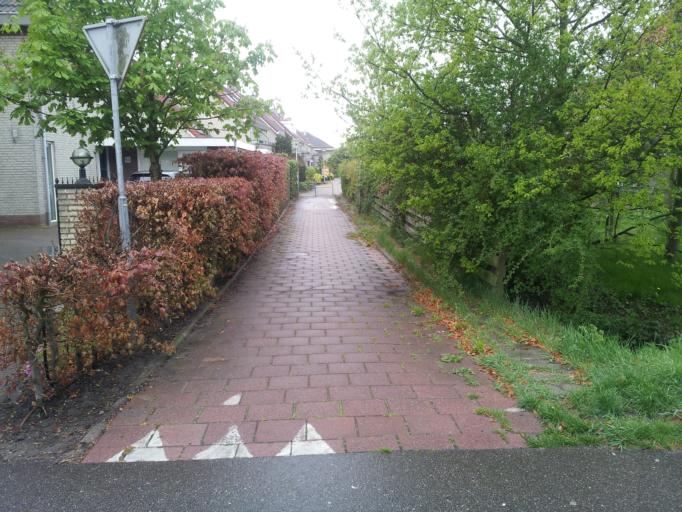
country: NL
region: South Holland
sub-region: Gemeente Pijnacker-Nootdorp
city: Pijnacker
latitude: 52.0420
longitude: 4.4081
